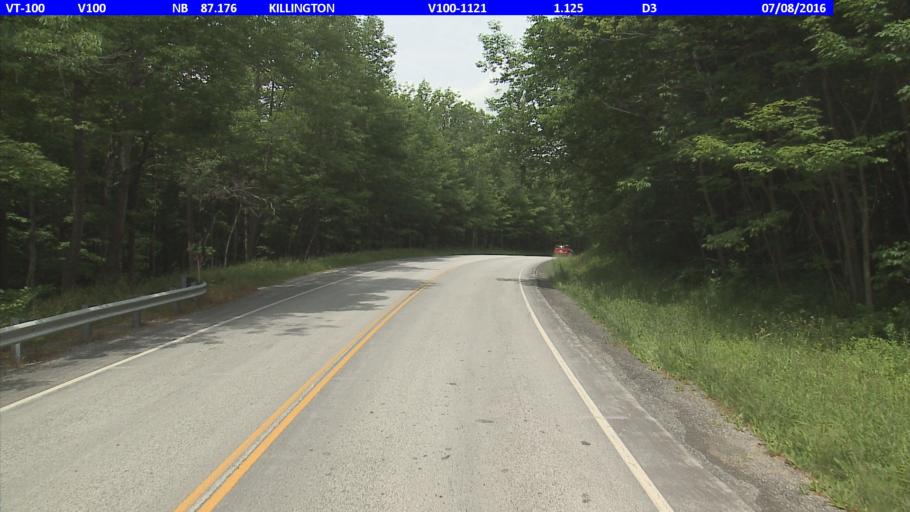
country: US
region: Vermont
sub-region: Rutland County
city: Rutland
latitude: 43.6823
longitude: -72.8131
